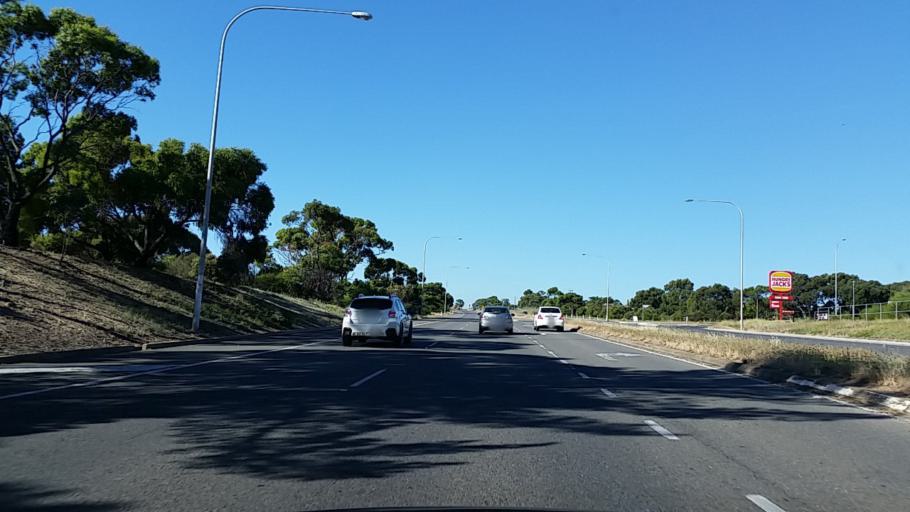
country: AU
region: South Australia
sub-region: Marion
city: Happy Valley
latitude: -35.0757
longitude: 138.5213
